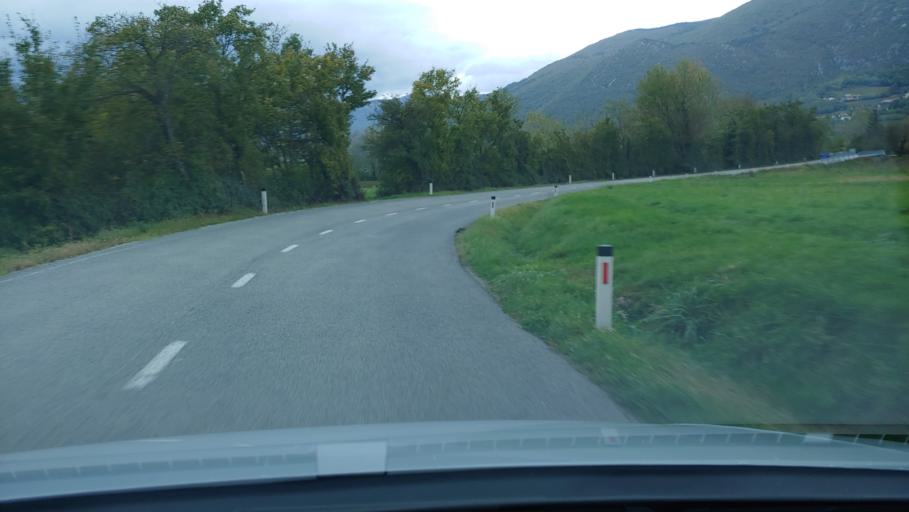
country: SI
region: Vipava
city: Vipava
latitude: 45.8238
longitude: 13.9452
